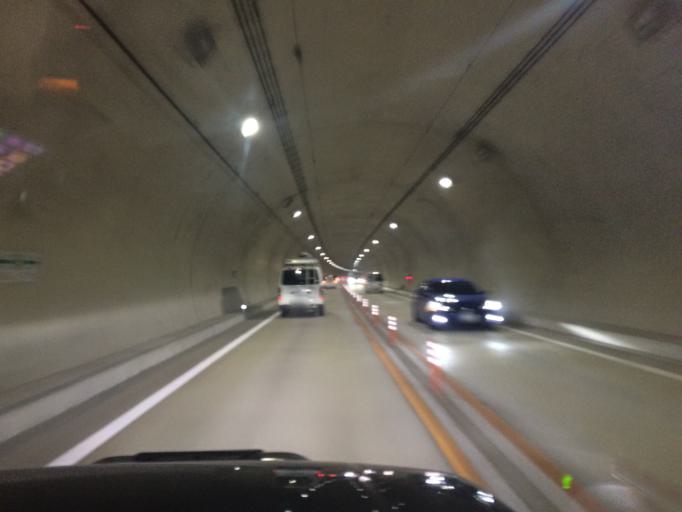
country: JP
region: Tottori
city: Tottori
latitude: 35.5023
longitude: 134.1051
